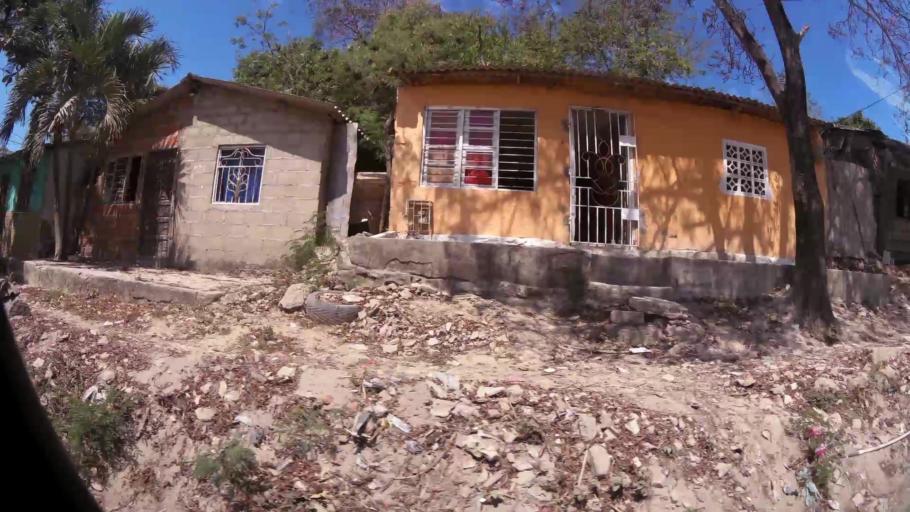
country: CO
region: Atlantico
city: Barranquilla
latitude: 10.9639
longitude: -74.8122
